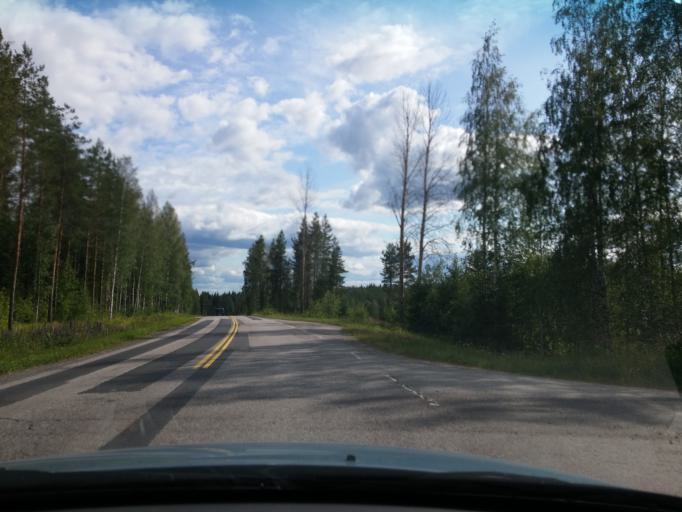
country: FI
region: Central Finland
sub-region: Keuruu
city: Keuruu
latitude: 62.3168
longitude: 24.7300
